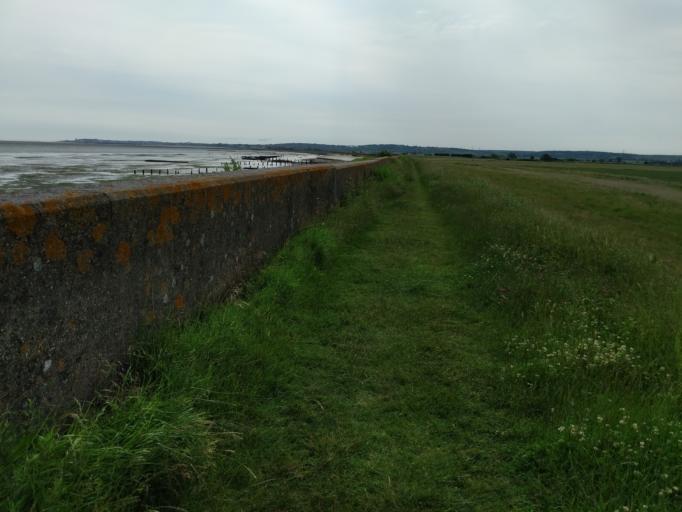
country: GB
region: England
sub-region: Kent
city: Leysdown-on-Sea
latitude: 51.3458
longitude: 0.9465
